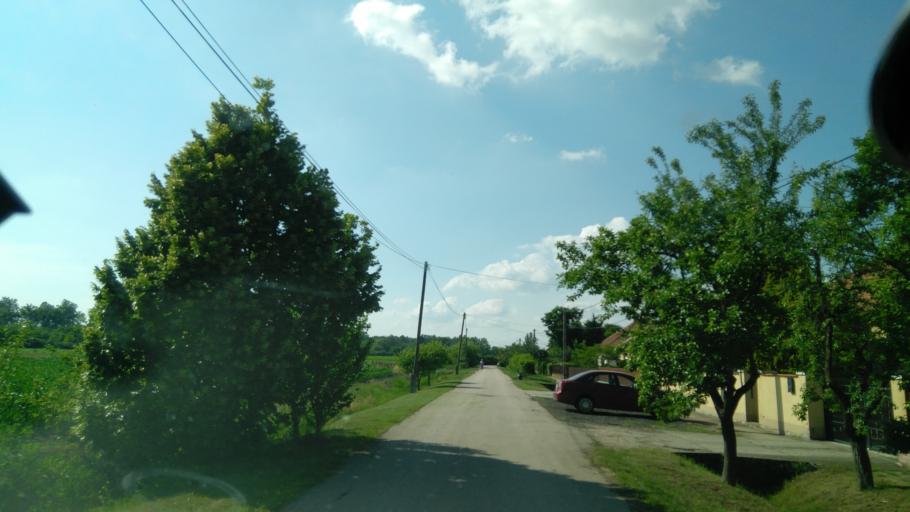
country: HU
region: Bekes
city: Bekes
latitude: 46.7032
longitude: 21.1769
